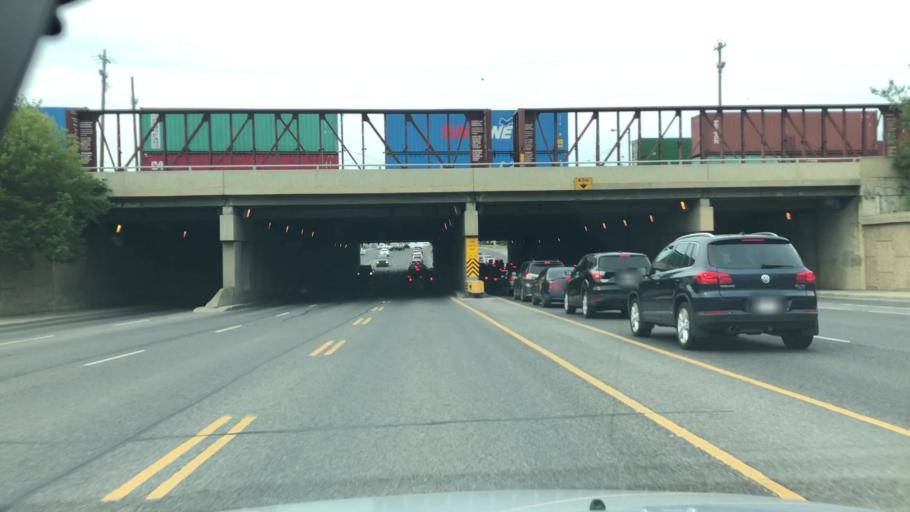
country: CA
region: Alberta
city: Edmonton
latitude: 53.5827
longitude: -113.4920
